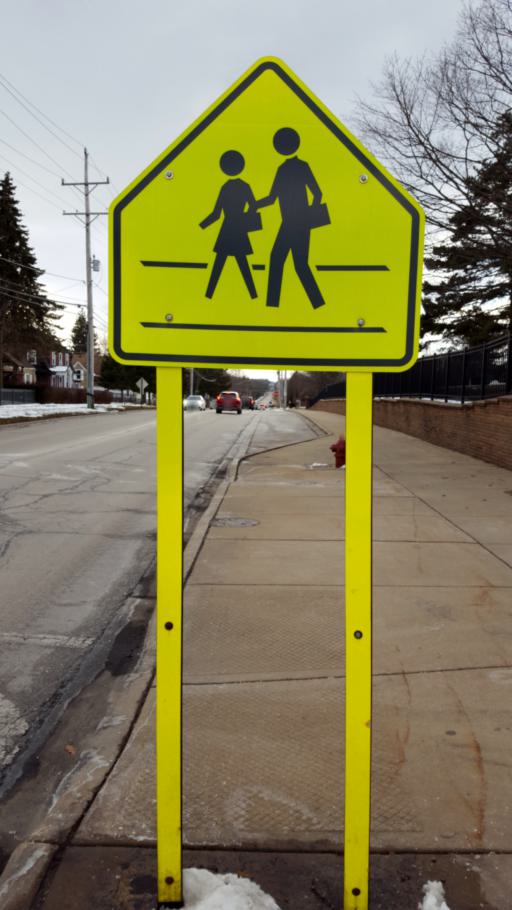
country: US
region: Illinois
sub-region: Lake County
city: Highwood
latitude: 42.1998
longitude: -87.8142
